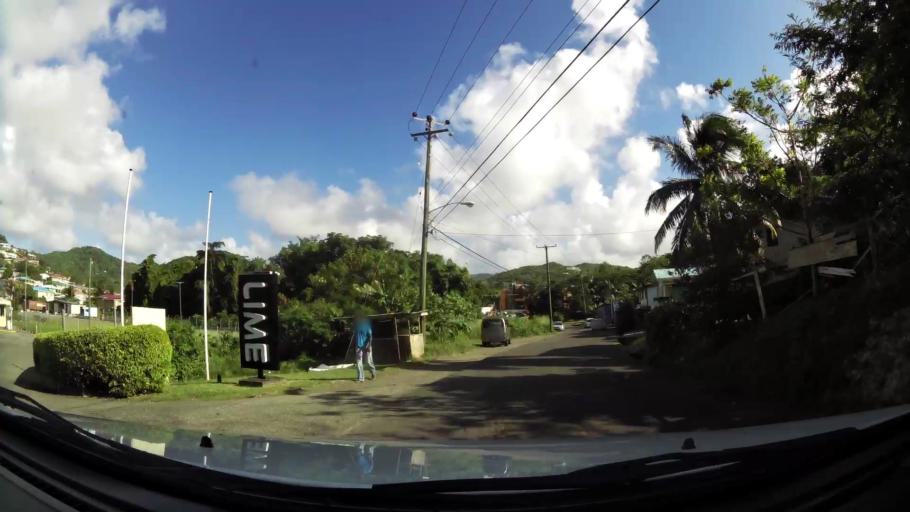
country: LC
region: Castries Quarter
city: Bisee
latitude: 14.0449
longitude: -60.9636
